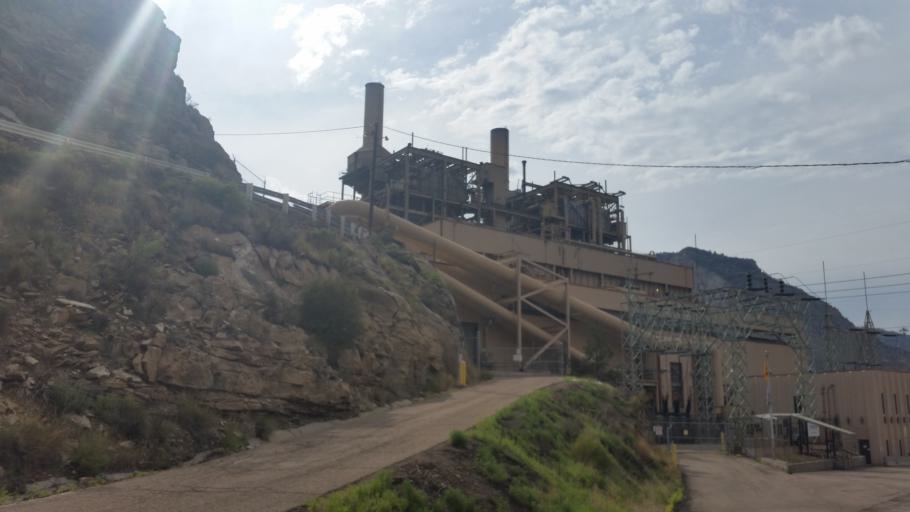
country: US
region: Utah
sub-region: Carbon County
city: Helper
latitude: 39.7261
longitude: -110.8622
